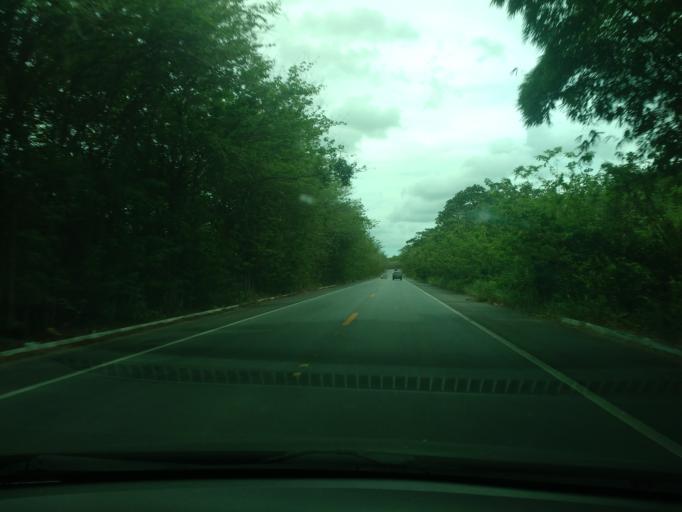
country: BR
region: Alagoas
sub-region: Murici
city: Murici
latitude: -9.2556
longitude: -35.9904
